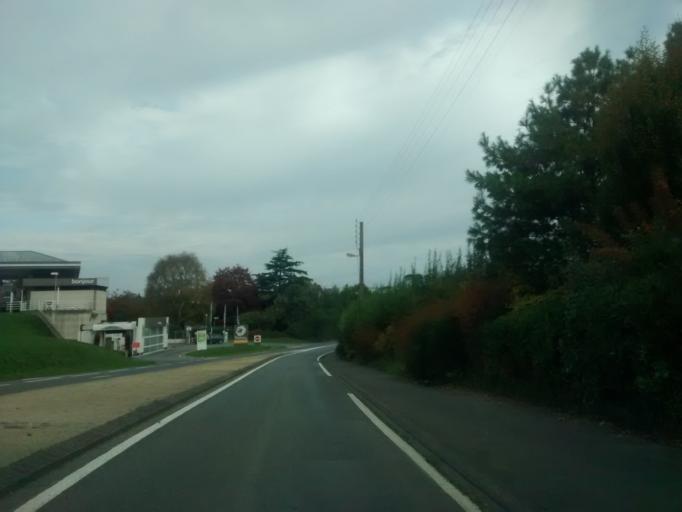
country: FR
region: Brittany
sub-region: Departement d'Ille-et-Vilaine
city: Dinard
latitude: 48.6209
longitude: -2.0577
